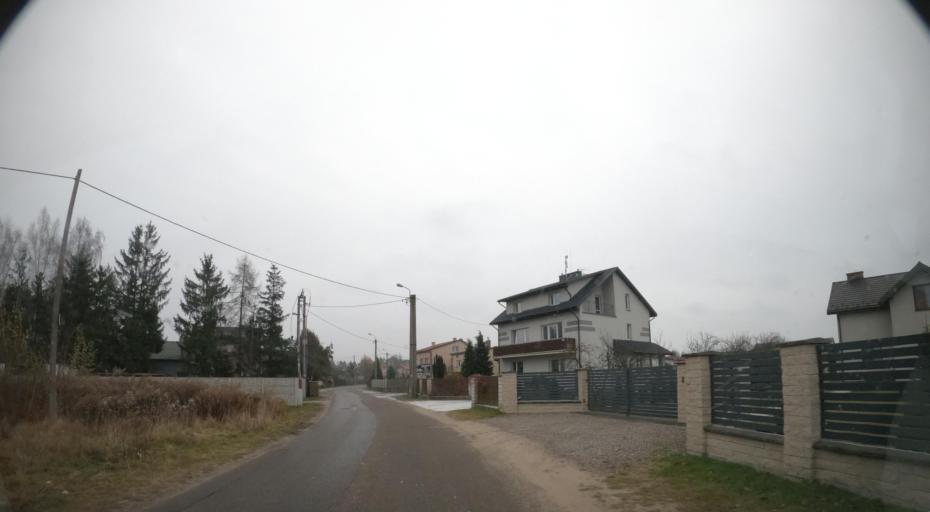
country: PL
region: Masovian Voivodeship
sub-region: Powiat radomski
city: Jedlnia-Letnisko
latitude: 51.4148
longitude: 21.2548
